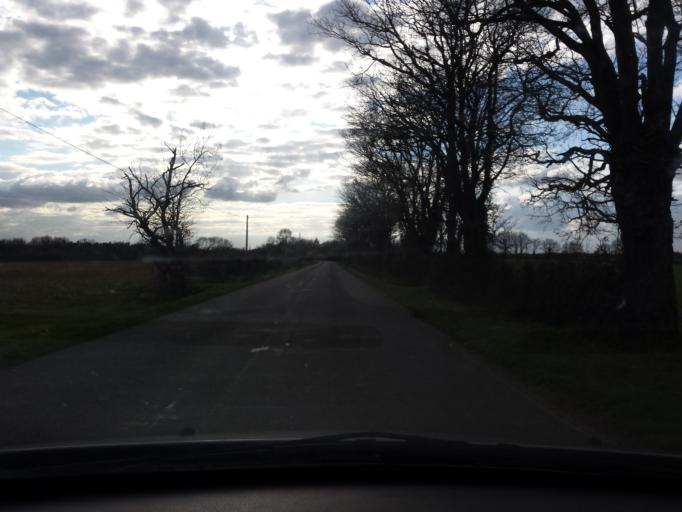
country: FR
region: Pays de la Loire
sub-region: Departement de la Vendee
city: Saint-Martin-des-Noyers
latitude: 46.7240
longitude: -1.1622
